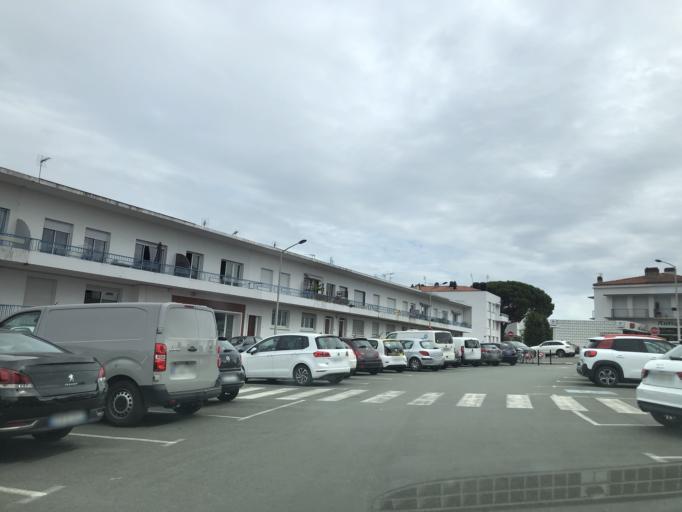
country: FR
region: Poitou-Charentes
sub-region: Departement de la Charente-Maritime
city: Royan
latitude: 45.6236
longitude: -1.0316
